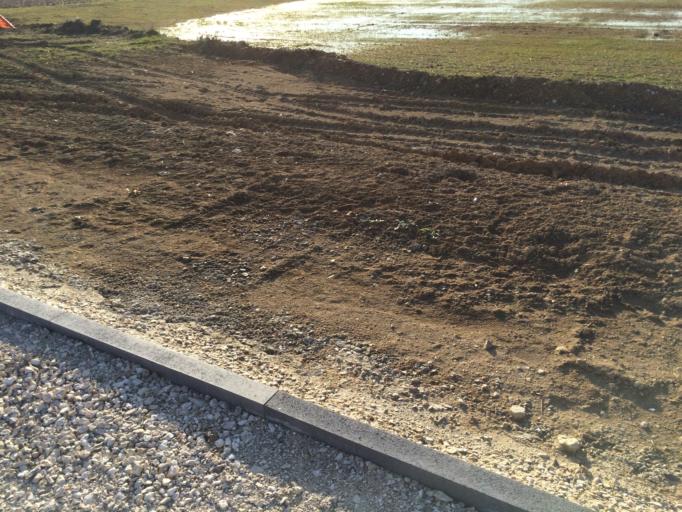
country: FR
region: Ile-de-France
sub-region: Departement de l'Essonne
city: Vauhallan
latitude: 48.7188
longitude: 2.1933
